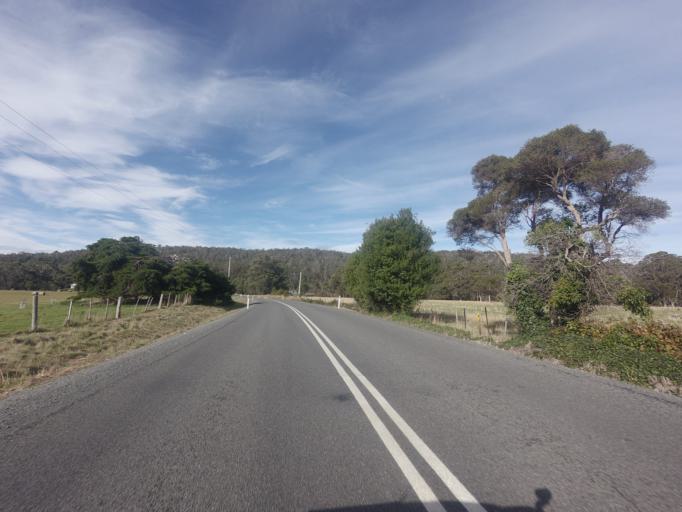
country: AU
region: Tasmania
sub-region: Clarence
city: Sandford
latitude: -43.0642
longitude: 147.8368
